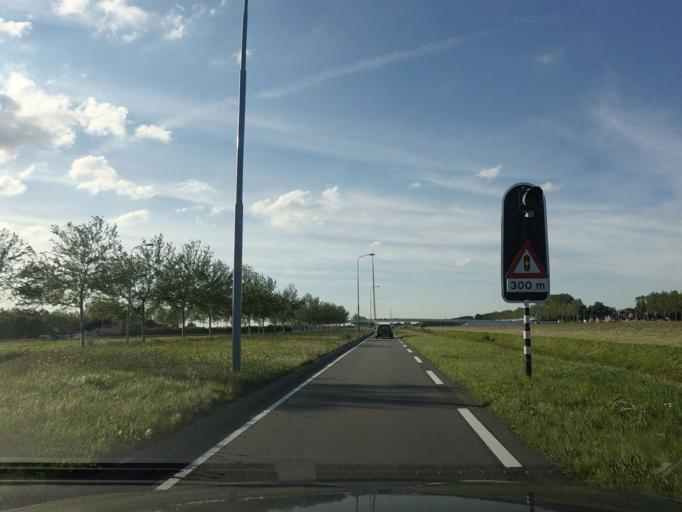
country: NL
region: North Holland
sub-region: Gemeente Haarlemmermeer
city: Hoofddorp
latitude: 52.2819
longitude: 4.6657
